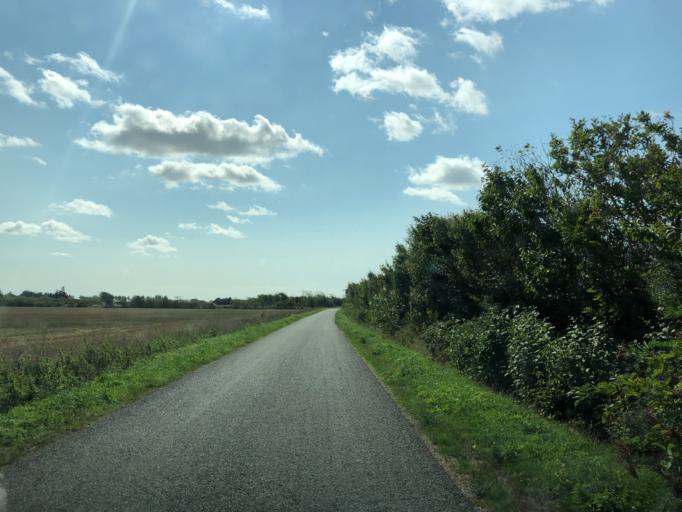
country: DK
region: Central Jutland
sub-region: Holstebro Kommune
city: Ulfborg
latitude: 56.2635
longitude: 8.1776
